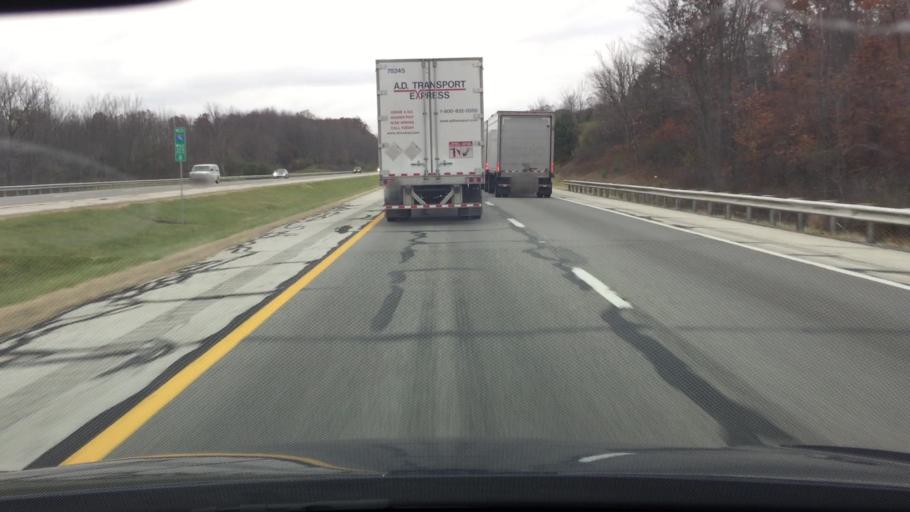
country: US
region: Ohio
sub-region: Mahoning County
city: Canfield
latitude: 41.0580
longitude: -80.7782
